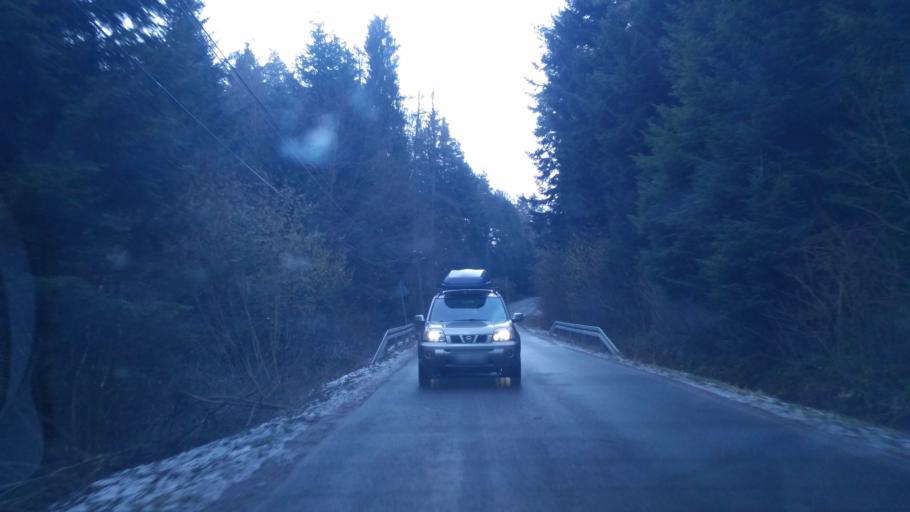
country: PL
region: Subcarpathian Voivodeship
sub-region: Powiat rzeszowski
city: Blazowa
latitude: 49.8581
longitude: 22.0971
